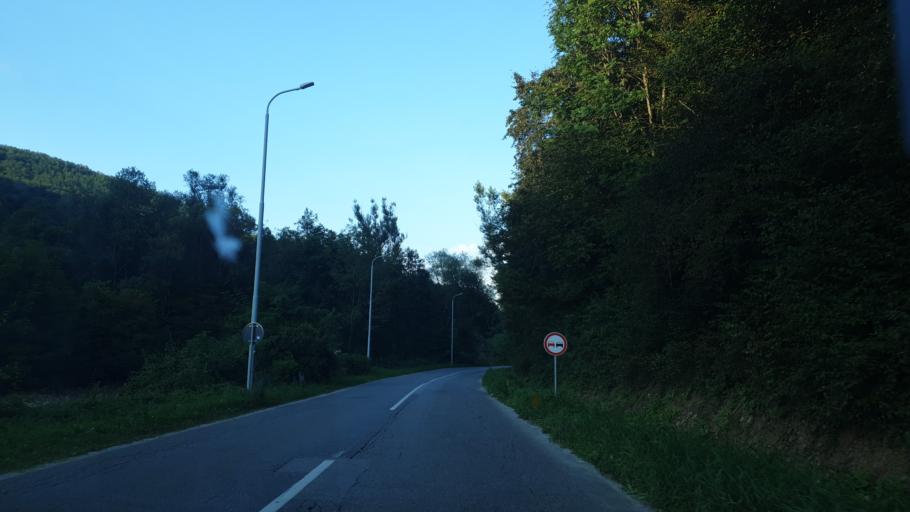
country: RS
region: Central Serbia
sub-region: Zlatiborski Okrug
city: Pozega
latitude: 43.9362
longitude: 20.0064
